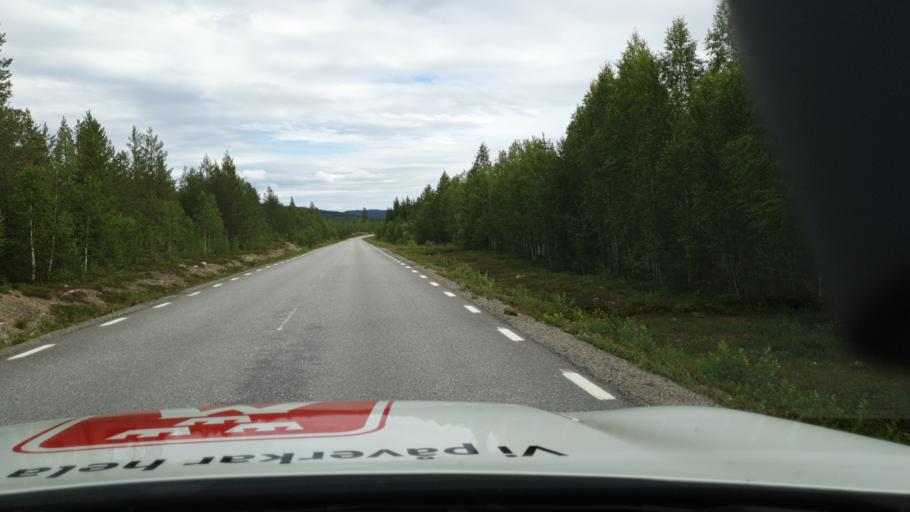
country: SE
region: Vaesterbotten
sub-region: Sorsele Kommun
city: Sorsele
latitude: 65.5110
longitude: 17.3040
